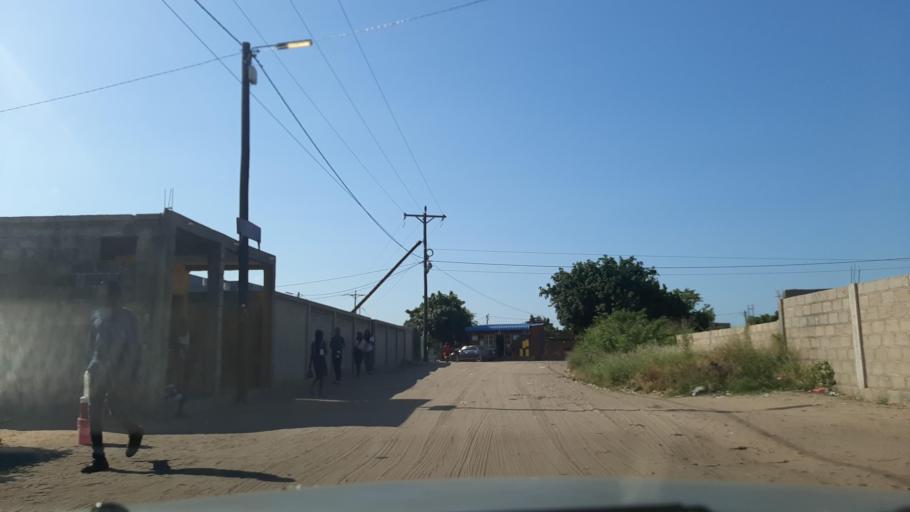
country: MZ
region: Maputo
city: Matola
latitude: -25.7907
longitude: 32.4879
